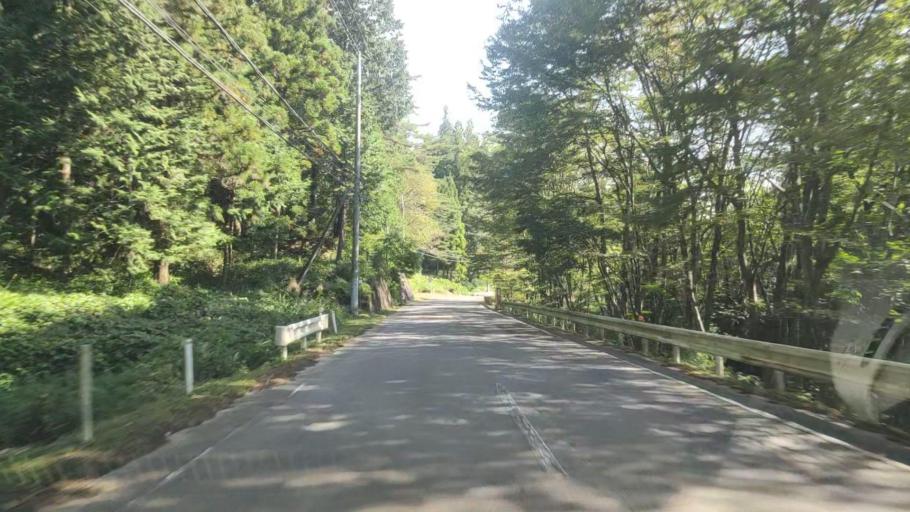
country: JP
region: Gunma
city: Nakanojomachi
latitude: 36.6158
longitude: 138.7419
